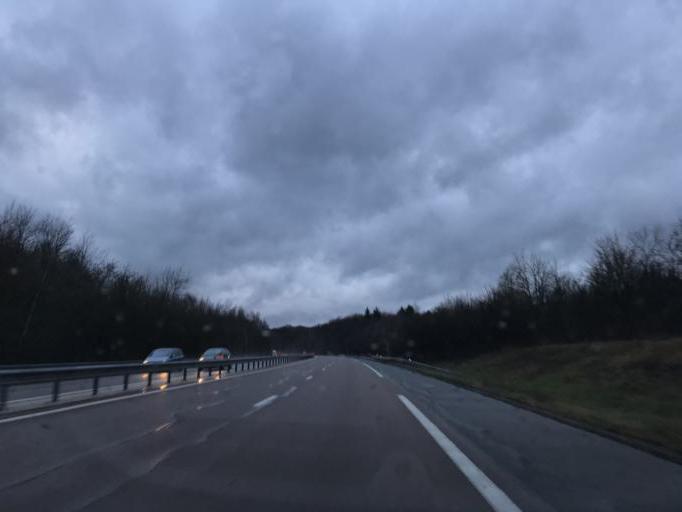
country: FR
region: Franche-Comte
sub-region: Departement du Jura
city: Foucherans
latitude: 47.0762
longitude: 5.4371
